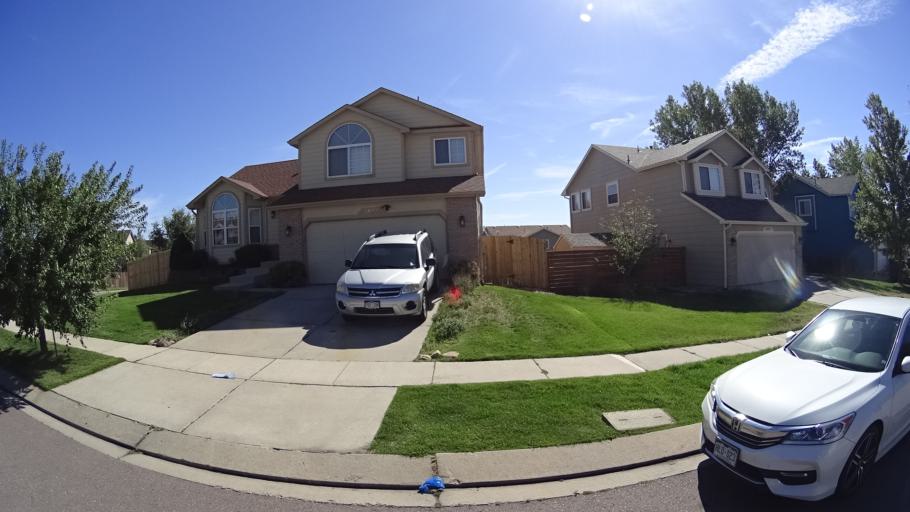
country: US
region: Colorado
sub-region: El Paso County
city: Black Forest
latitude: 38.9528
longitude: -104.7304
